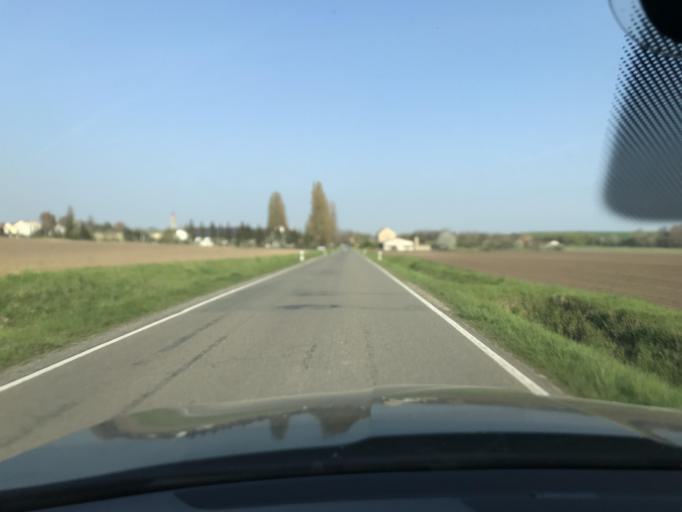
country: DE
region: Saxony-Anhalt
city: Schwanebeck
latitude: 51.9815
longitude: 11.0559
